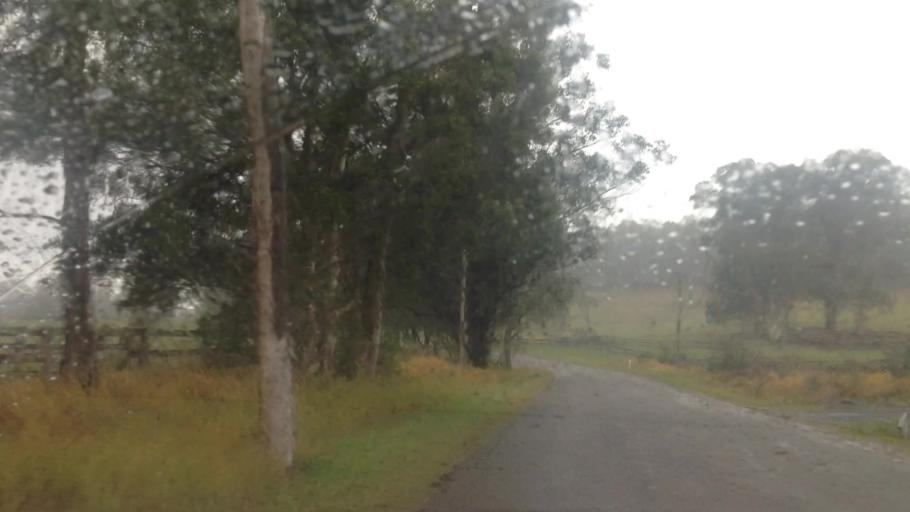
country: AU
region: New South Wales
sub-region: Wyong Shire
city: Little Jilliby
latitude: -33.1950
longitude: 151.3578
